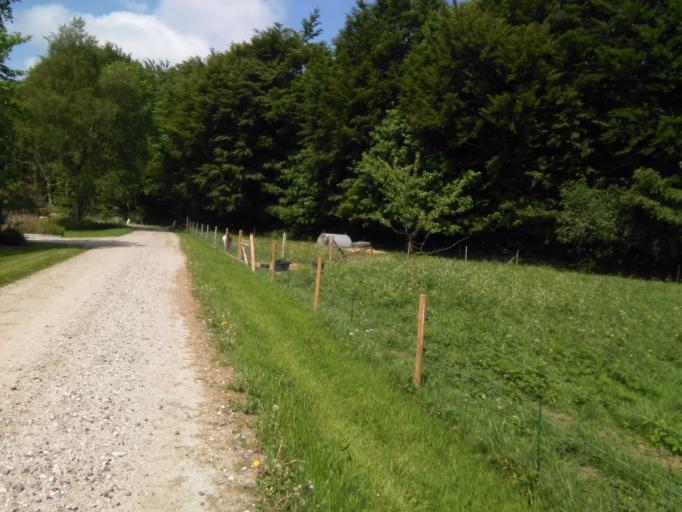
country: DK
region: Central Jutland
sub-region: Arhus Kommune
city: Sabro
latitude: 56.2682
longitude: 9.9576
